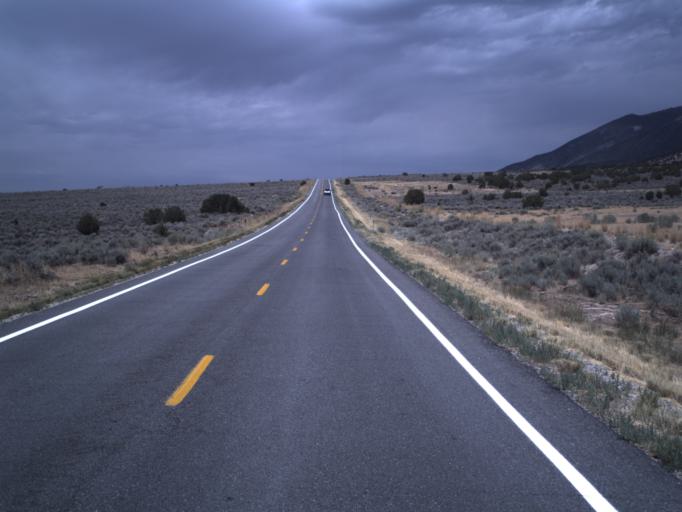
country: US
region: Utah
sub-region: Tooele County
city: Tooele
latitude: 40.3077
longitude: -112.2799
